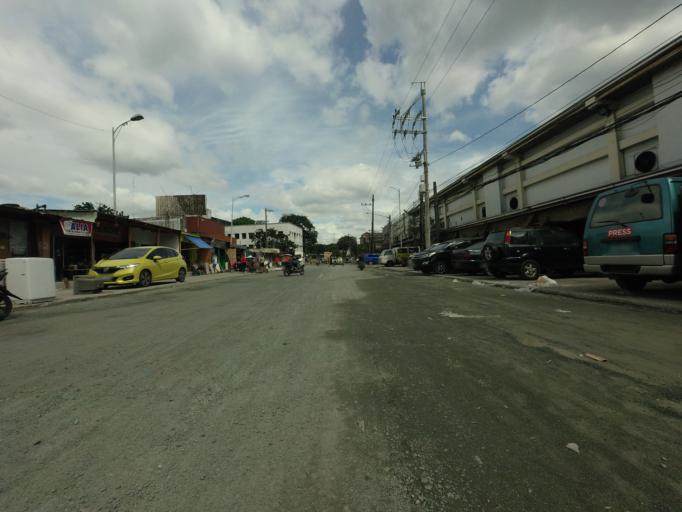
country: PH
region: Metro Manila
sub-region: City of Manila
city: Port Area
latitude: 14.5898
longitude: 120.9696
